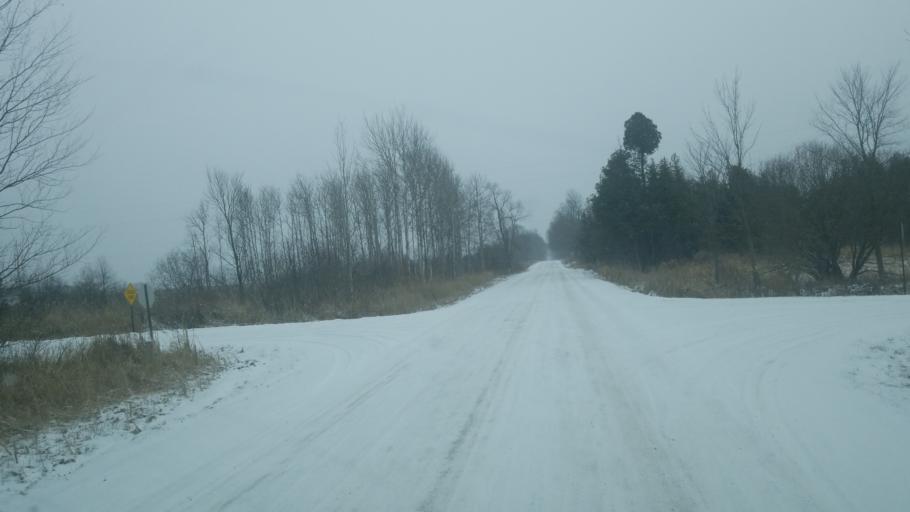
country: US
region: Michigan
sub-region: Osceola County
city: Reed City
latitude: 43.8436
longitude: -85.3940
